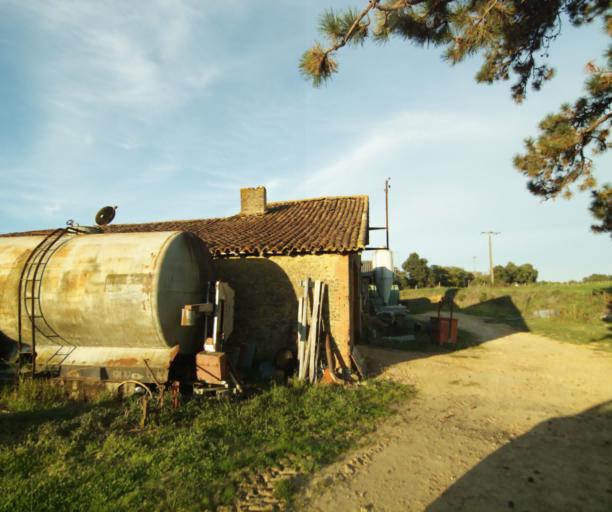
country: FR
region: Midi-Pyrenees
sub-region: Departement du Gers
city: Eauze
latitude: 43.8792
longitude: 0.0104
